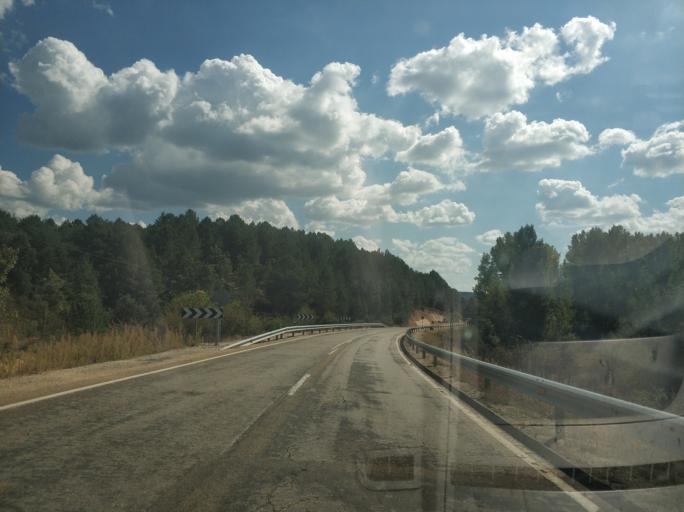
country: ES
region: Castille and Leon
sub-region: Provincia de Soria
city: Casarejos
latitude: 41.8022
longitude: -3.0428
